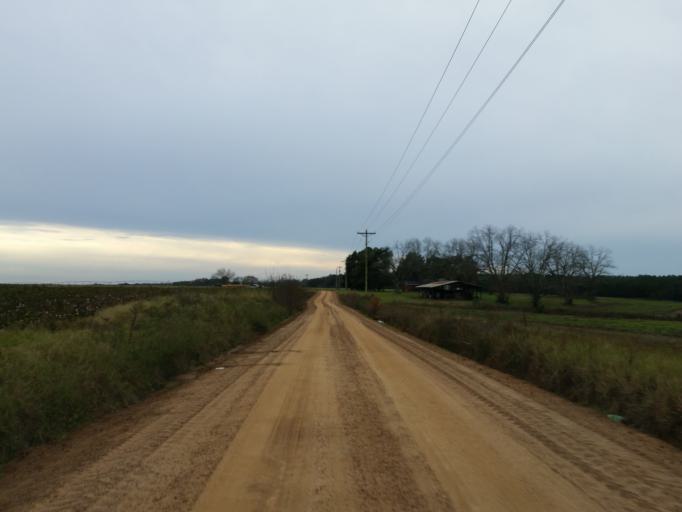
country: US
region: Georgia
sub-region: Crisp County
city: Cordele
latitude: 31.8984
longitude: -83.7146
